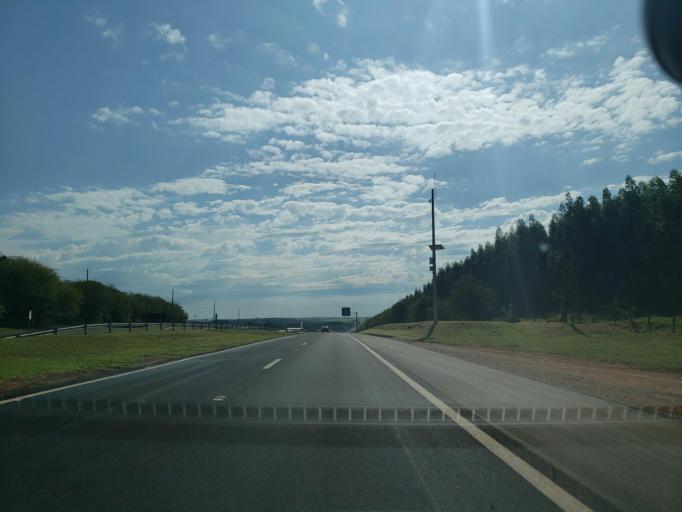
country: BR
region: Sao Paulo
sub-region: Pirajui
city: Pirajui
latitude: -21.9982
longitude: -49.4330
